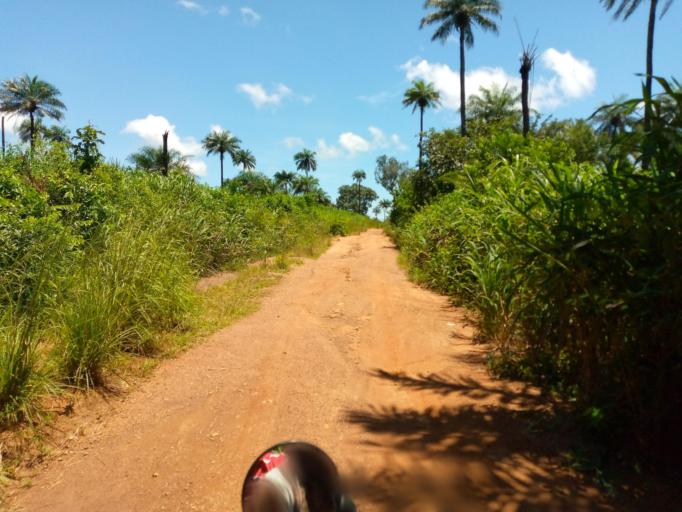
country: SL
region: Northern Province
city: Binkolo
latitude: 9.1166
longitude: -12.1762
